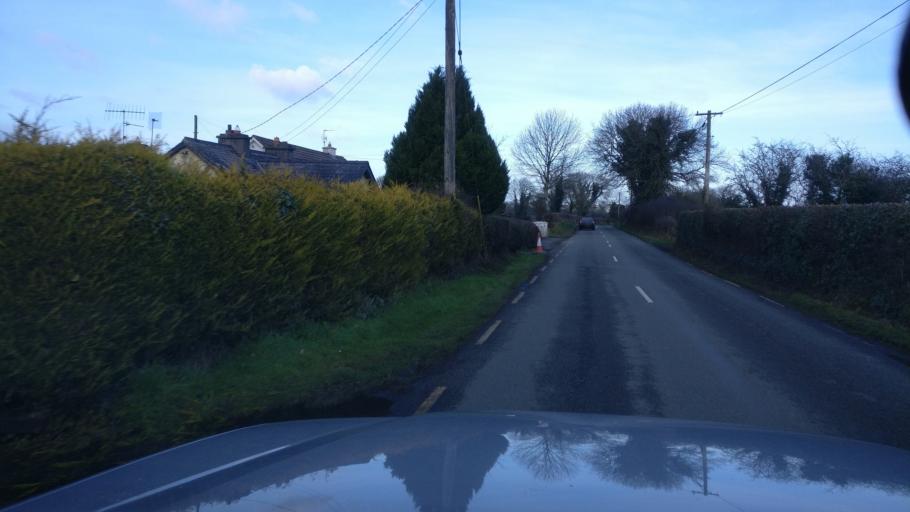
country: IE
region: Leinster
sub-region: Kilkenny
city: Castlecomer
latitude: 52.8472
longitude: -7.1783
